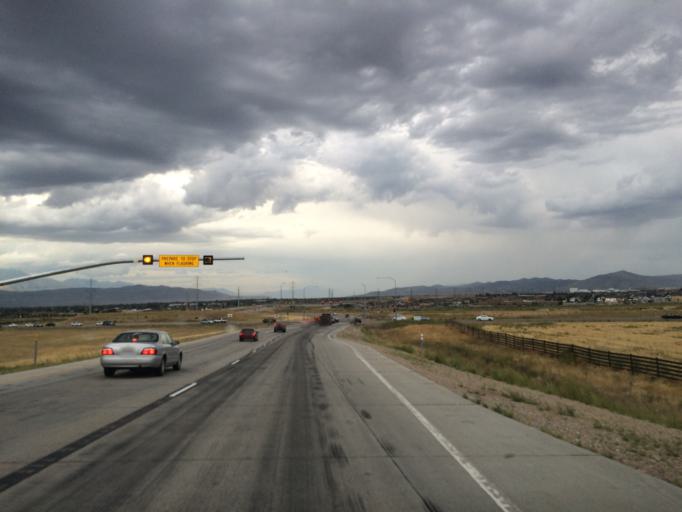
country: US
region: Utah
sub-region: Salt Lake County
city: Oquirrh
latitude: 40.6112
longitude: -112.0367
